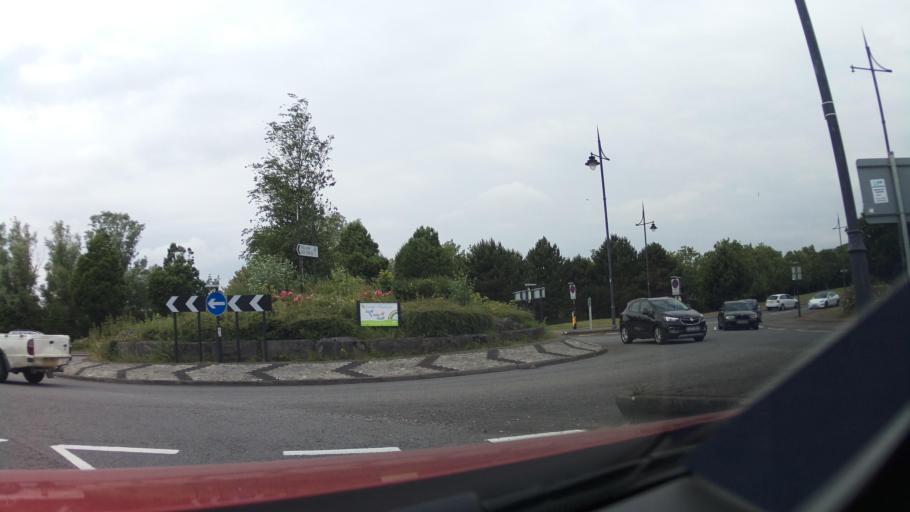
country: GB
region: Wales
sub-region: Vale of Glamorgan
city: Barry
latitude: 51.4008
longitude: -3.2730
